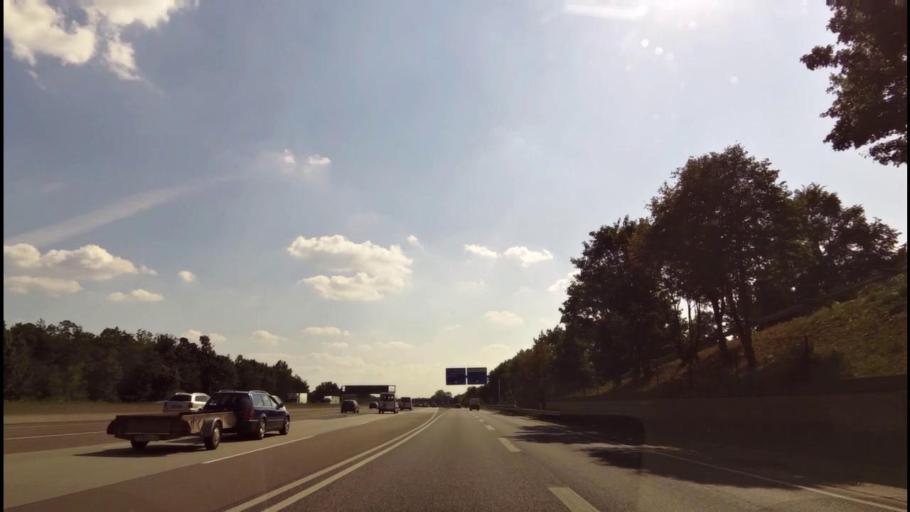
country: DE
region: Hesse
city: Morfelden-Walldorf
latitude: 50.0390
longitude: 8.5968
